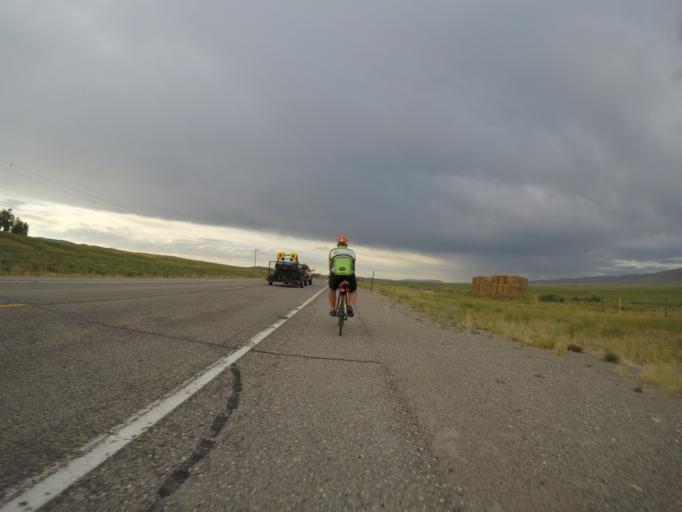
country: US
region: Utah
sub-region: Rich County
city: Randolph
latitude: 42.0481
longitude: -110.9314
